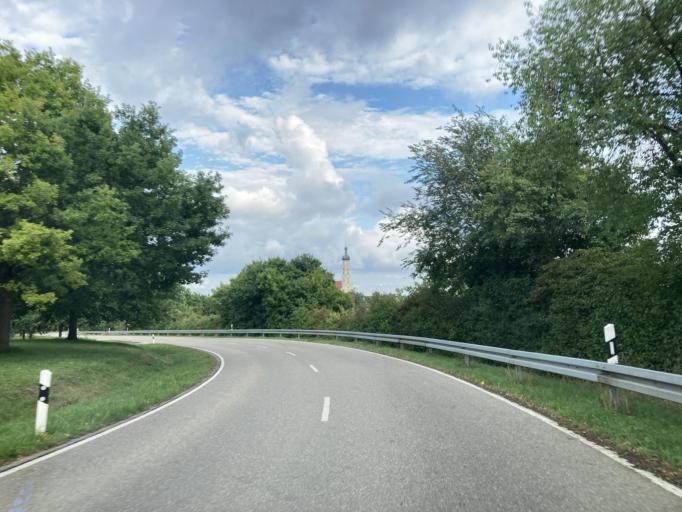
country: DE
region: Bavaria
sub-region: Swabia
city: Medlingen
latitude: 48.5703
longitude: 10.3131
